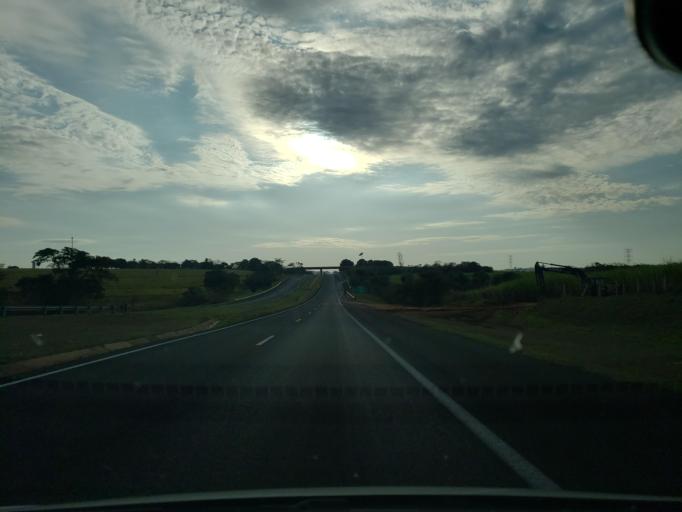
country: BR
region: Sao Paulo
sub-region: Mirandopolis
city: Mirandopolis
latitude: -21.0893
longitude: -51.0578
